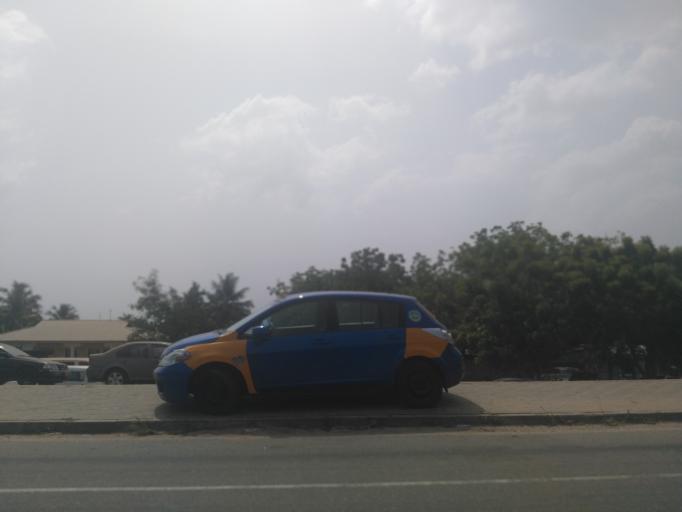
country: GH
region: Greater Accra
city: Dome
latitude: 5.6159
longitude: -0.2072
